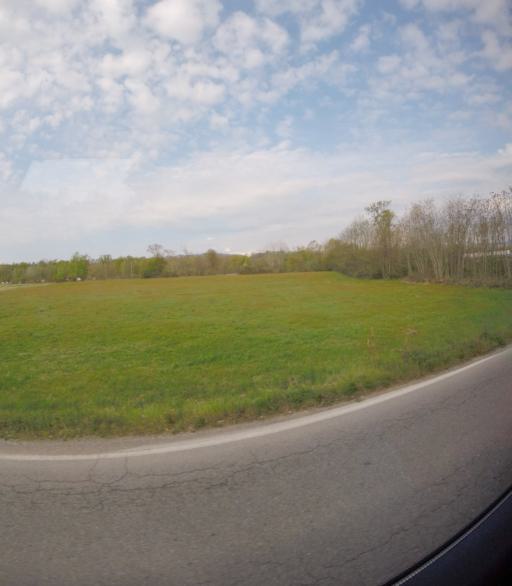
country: IT
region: Piedmont
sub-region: Provincia di Novara
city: Briga Novarese
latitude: 45.7243
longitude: 8.4464
